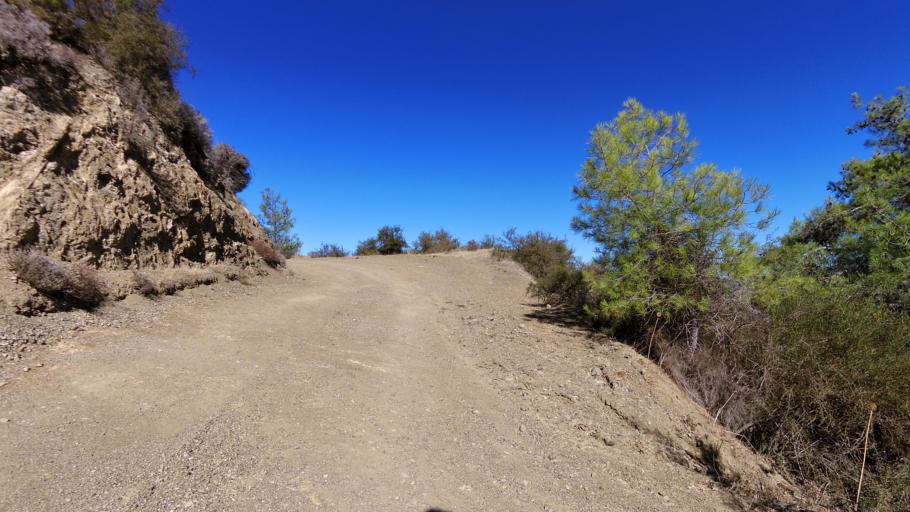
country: CY
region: Pafos
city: Polis
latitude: 35.0135
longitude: 32.4865
